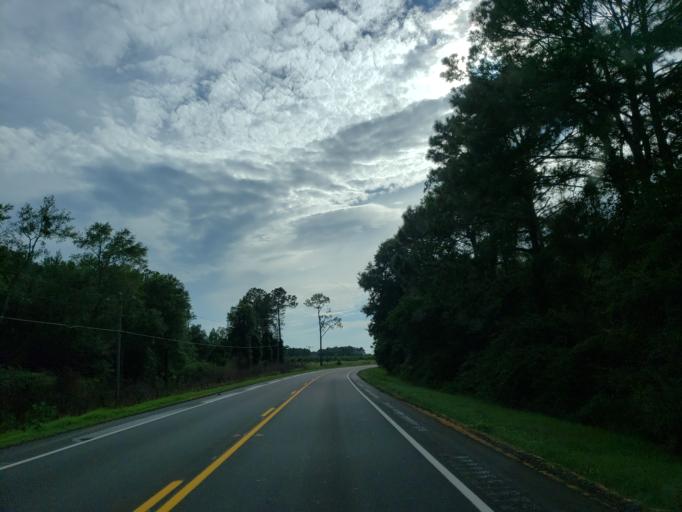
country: US
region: Georgia
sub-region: Irwin County
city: Ocilla
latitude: 31.5634
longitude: -83.3249
